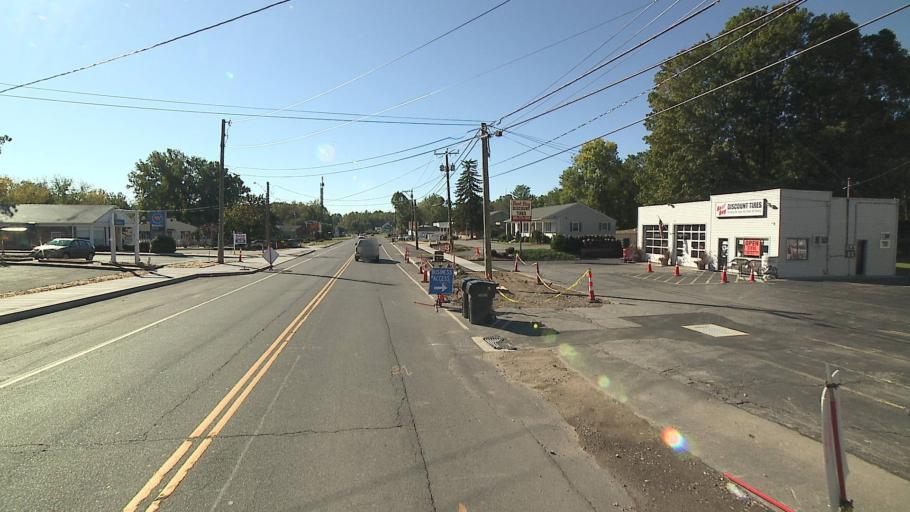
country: US
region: Connecticut
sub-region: Litchfield County
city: New Milford
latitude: 41.4812
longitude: -73.4093
